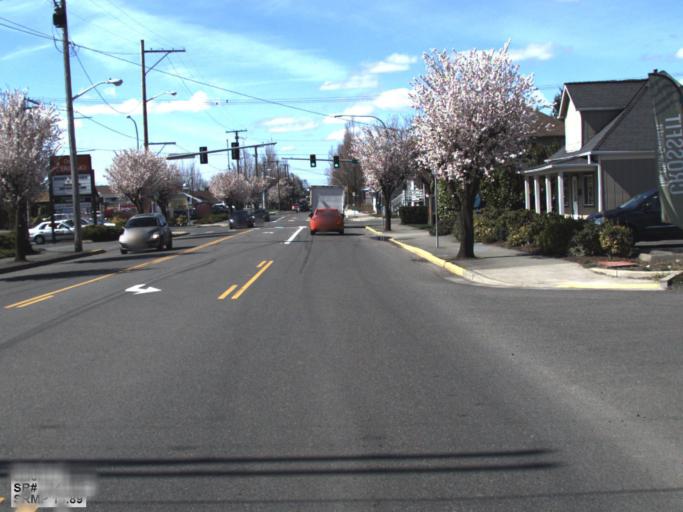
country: US
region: Washington
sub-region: King County
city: Enumclaw
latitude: 47.2014
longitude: -121.9852
